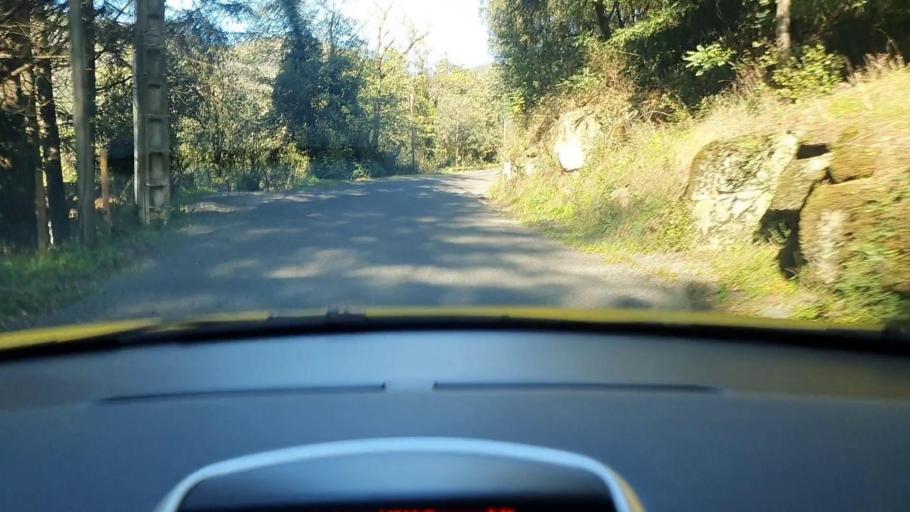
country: FR
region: Languedoc-Roussillon
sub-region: Departement du Gard
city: Valleraugue
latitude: 44.0347
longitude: 3.6786
